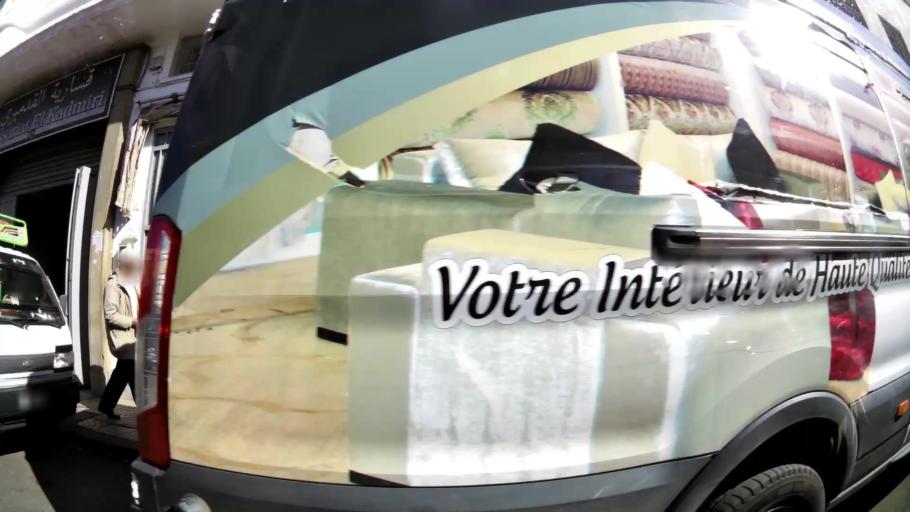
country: MA
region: Grand Casablanca
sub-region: Casablanca
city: Casablanca
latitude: 33.5910
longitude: -7.6101
